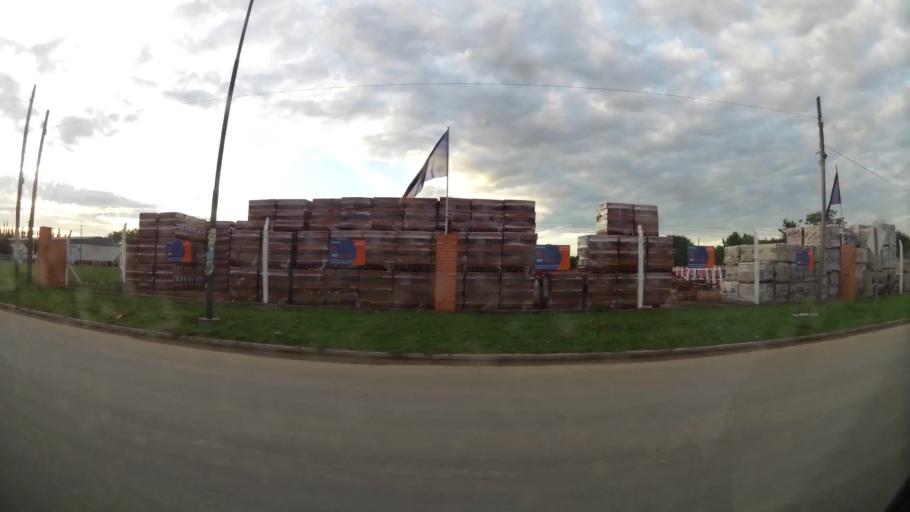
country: AR
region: Buenos Aires
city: San Nicolas de los Arroyos
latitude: -33.3206
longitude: -60.2432
